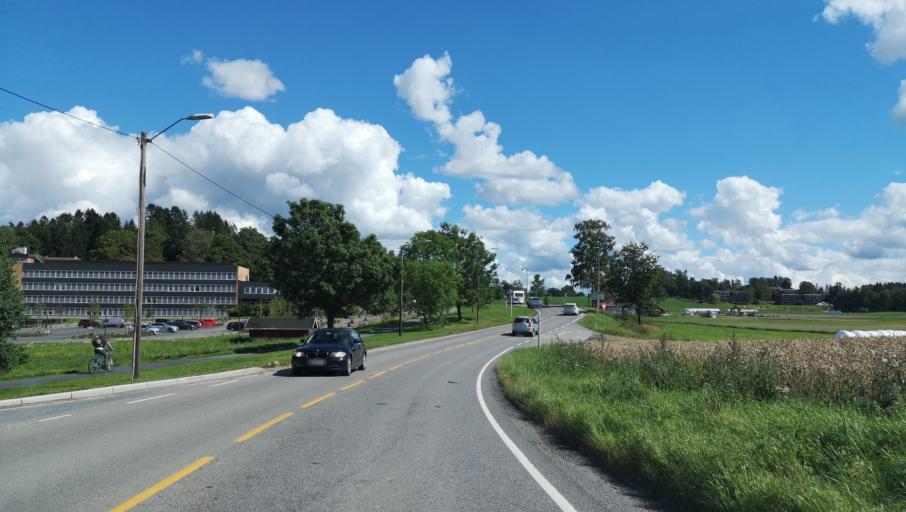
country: NO
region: Akershus
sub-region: As
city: As
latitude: 59.6648
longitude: 10.7566
